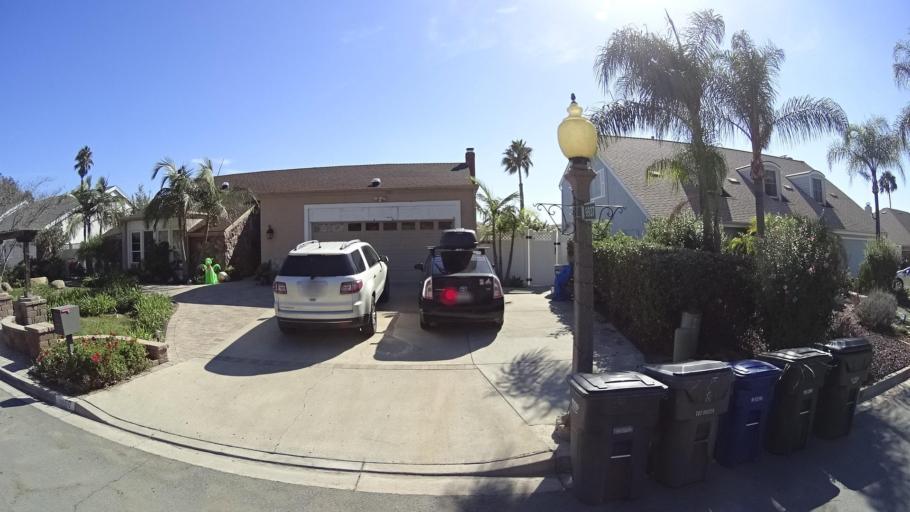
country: US
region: California
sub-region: San Diego County
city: Casa de Oro-Mount Helix
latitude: 32.7569
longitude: -116.9815
